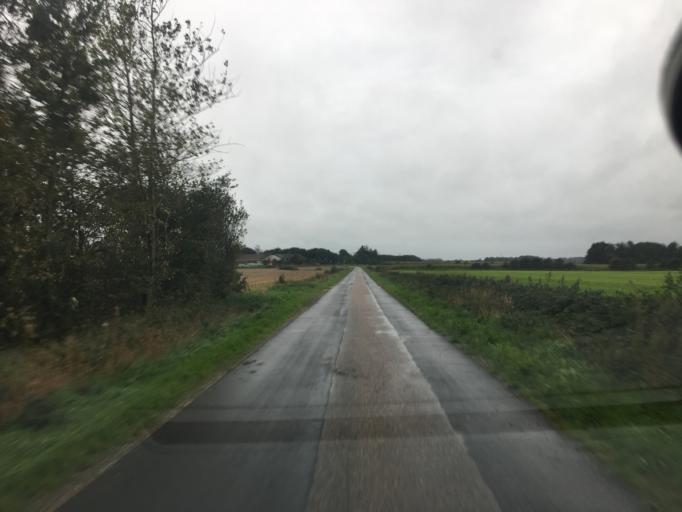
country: DE
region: Schleswig-Holstein
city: Ellhoft
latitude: 54.9445
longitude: 8.9975
